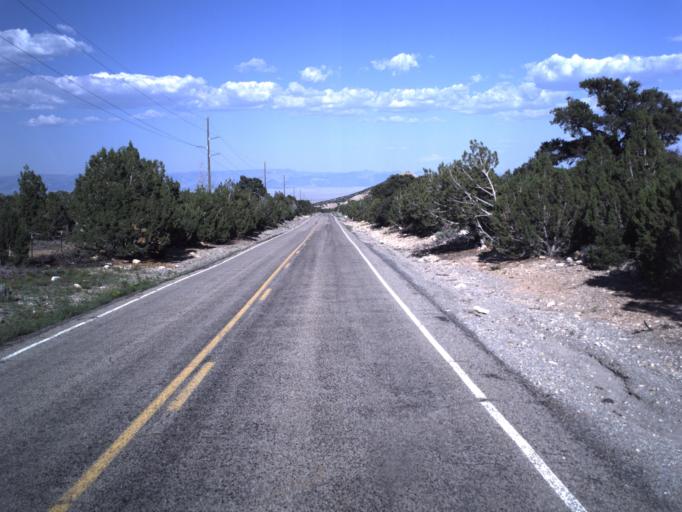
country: US
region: Utah
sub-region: Emery County
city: Huntington
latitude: 39.4841
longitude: -110.9787
